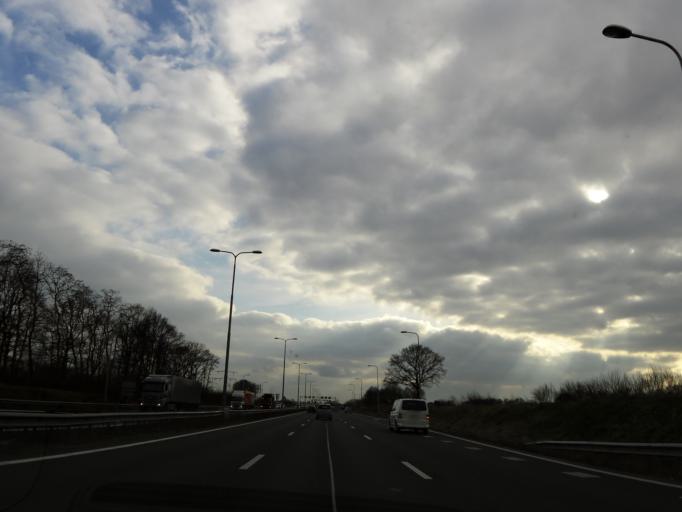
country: NL
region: Limburg
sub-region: Gemeente Stein
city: Urmond
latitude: 50.9958
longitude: 5.7873
